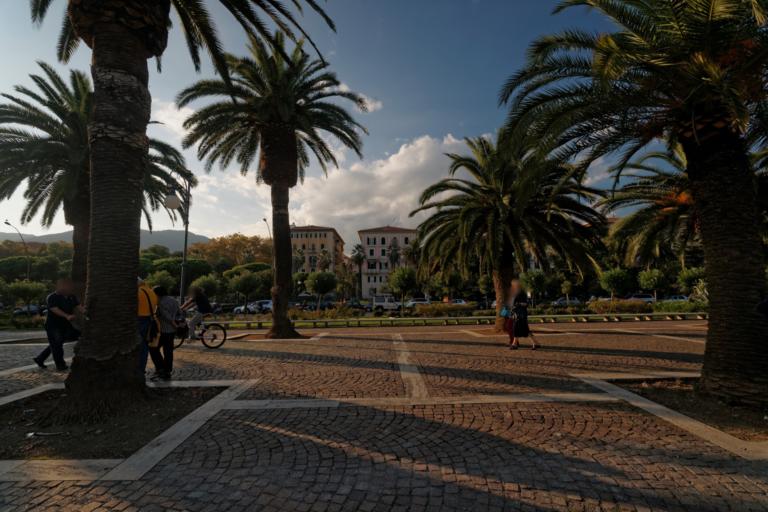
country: IT
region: Liguria
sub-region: Provincia di La Spezia
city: La Spezia
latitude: 44.1034
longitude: 9.8259
